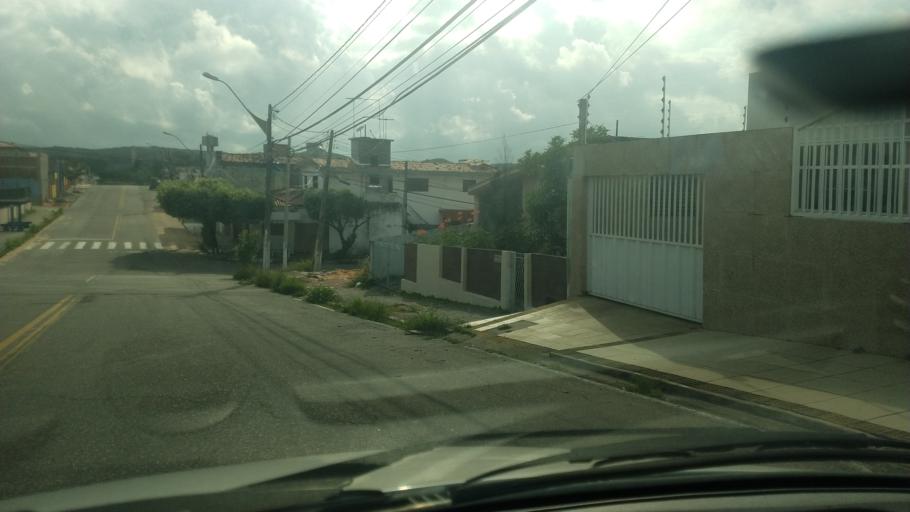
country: BR
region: Rio Grande do Norte
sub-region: Natal
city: Natal
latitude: -5.8426
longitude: -35.2064
